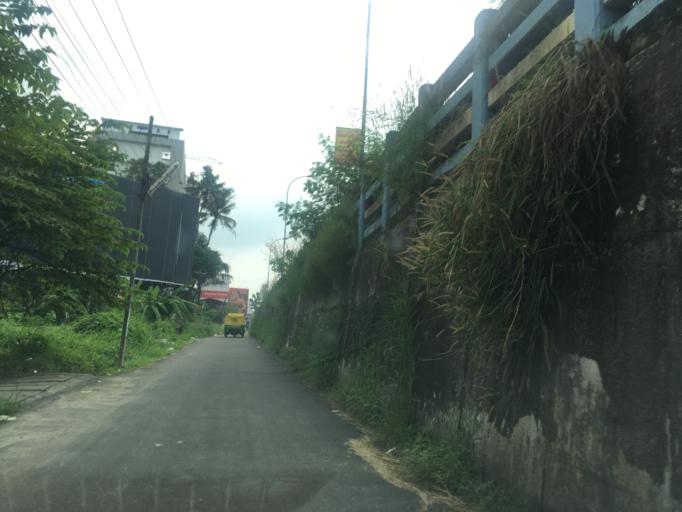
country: IN
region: Kerala
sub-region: Ernakulam
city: Elur
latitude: 10.0320
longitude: 76.3047
